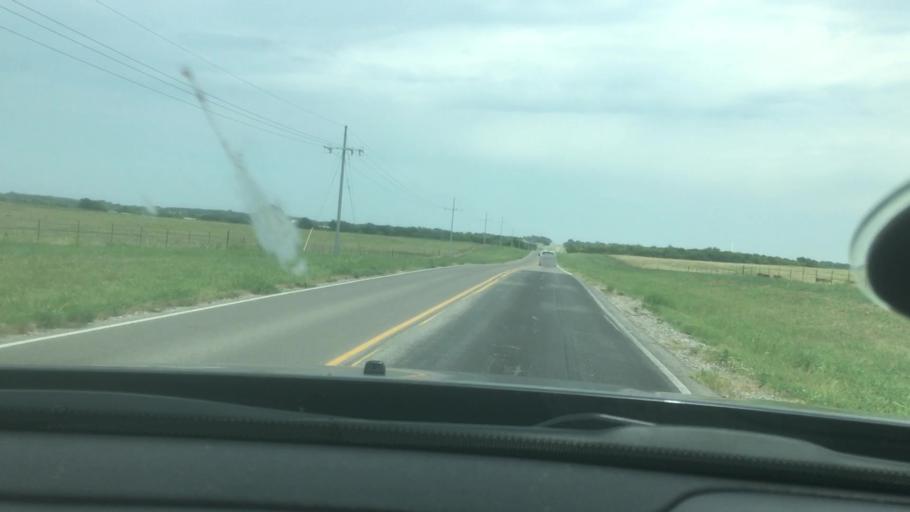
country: US
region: Oklahoma
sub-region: Murray County
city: Davis
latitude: 34.4772
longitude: -97.0809
